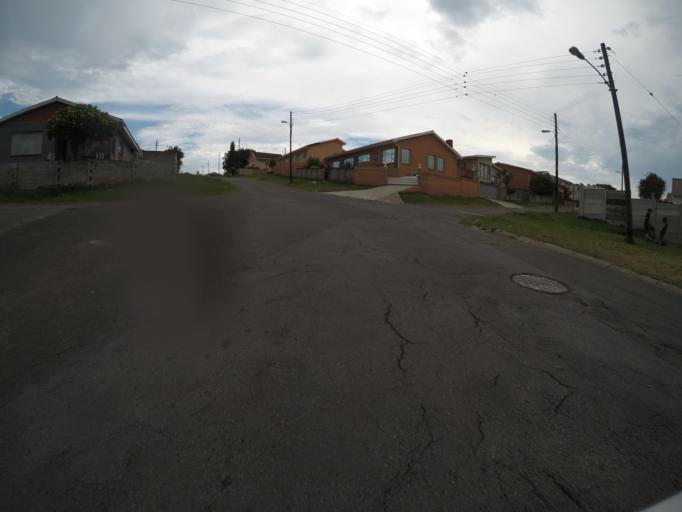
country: ZA
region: Eastern Cape
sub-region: Buffalo City Metropolitan Municipality
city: East London
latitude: -33.0221
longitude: 27.8669
